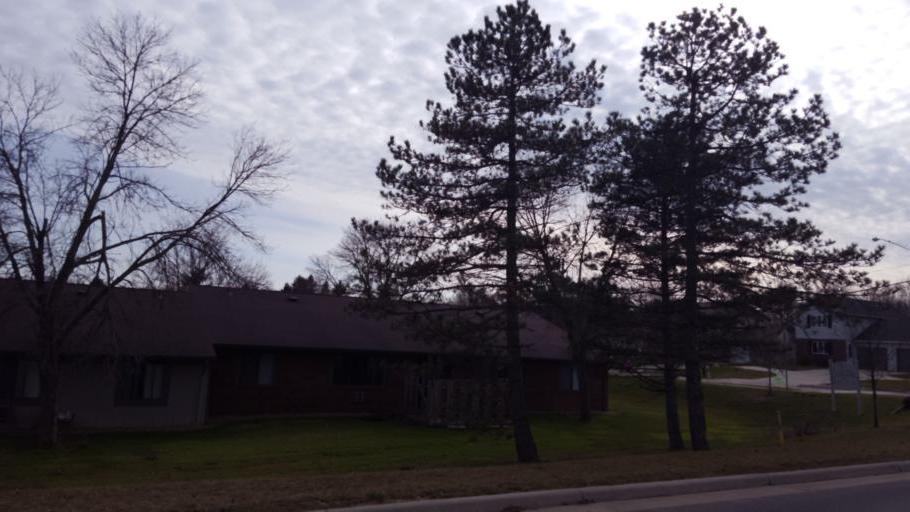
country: US
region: Ohio
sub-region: Richland County
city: Mansfield
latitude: 40.7107
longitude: -82.5362
